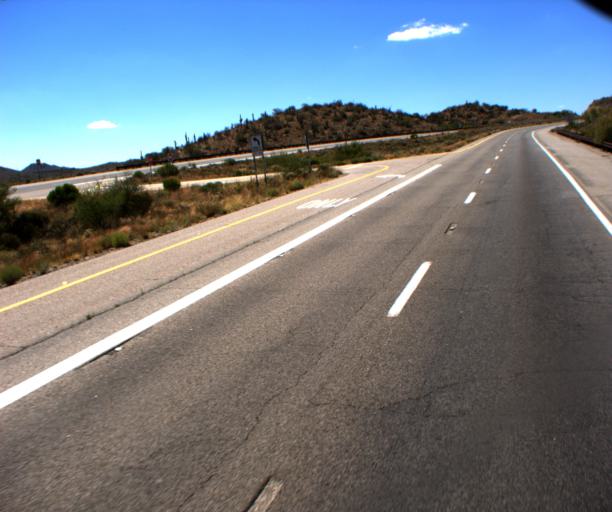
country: US
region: Arizona
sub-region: Yavapai County
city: Bagdad
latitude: 34.4513
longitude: -113.2864
